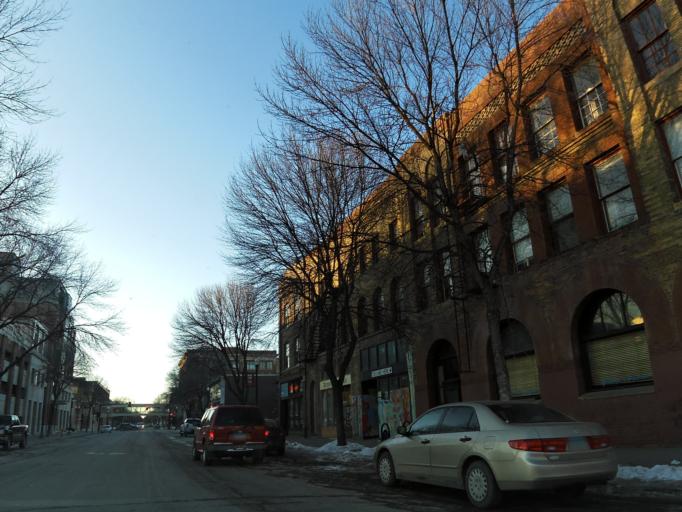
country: US
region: North Dakota
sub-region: Grand Forks County
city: Grand Forks
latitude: 47.9236
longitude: -97.0301
